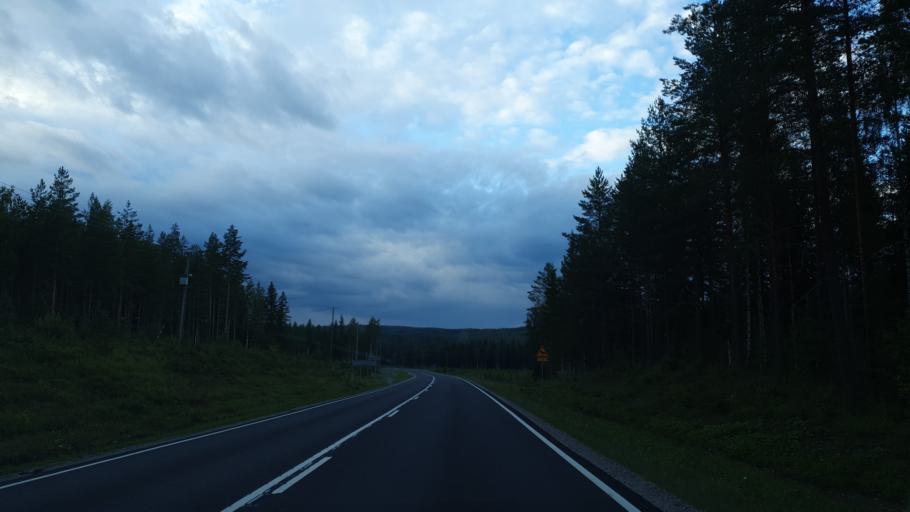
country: FI
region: North Karelia
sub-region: Pielisen Karjala
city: Lieksa
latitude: 63.2415
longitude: 30.1346
